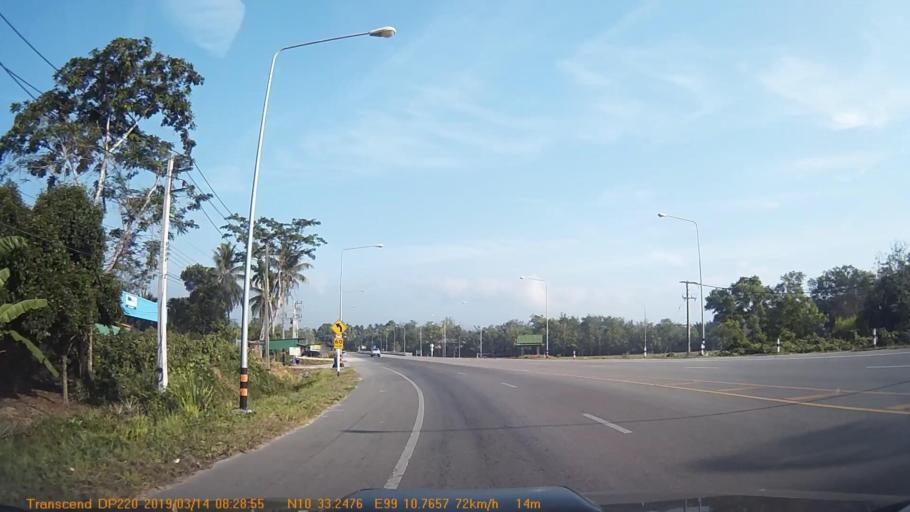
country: TH
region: Chumphon
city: Chumphon
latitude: 10.5541
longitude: 99.1794
